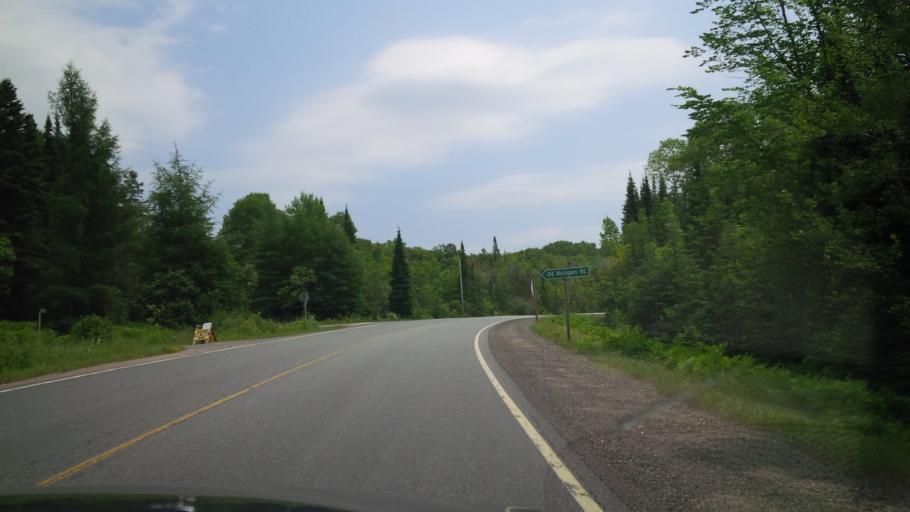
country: CA
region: Ontario
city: Huntsville
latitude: 45.5324
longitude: -79.3048
